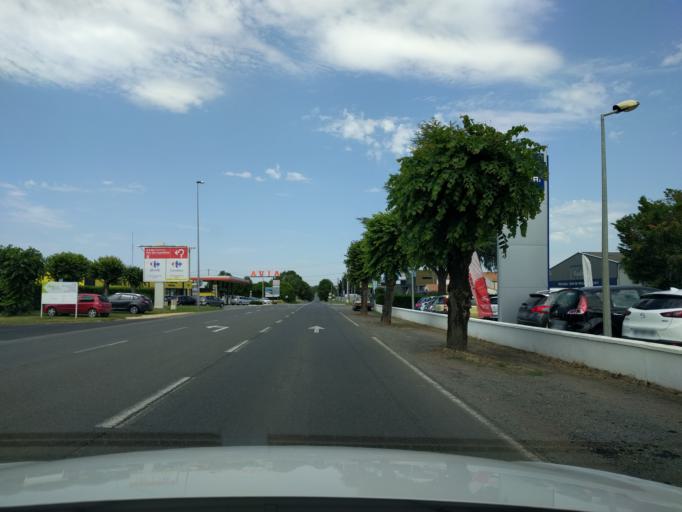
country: FR
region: Poitou-Charentes
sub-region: Departement des Deux-Sevres
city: Niort
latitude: 46.3415
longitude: -0.4906
